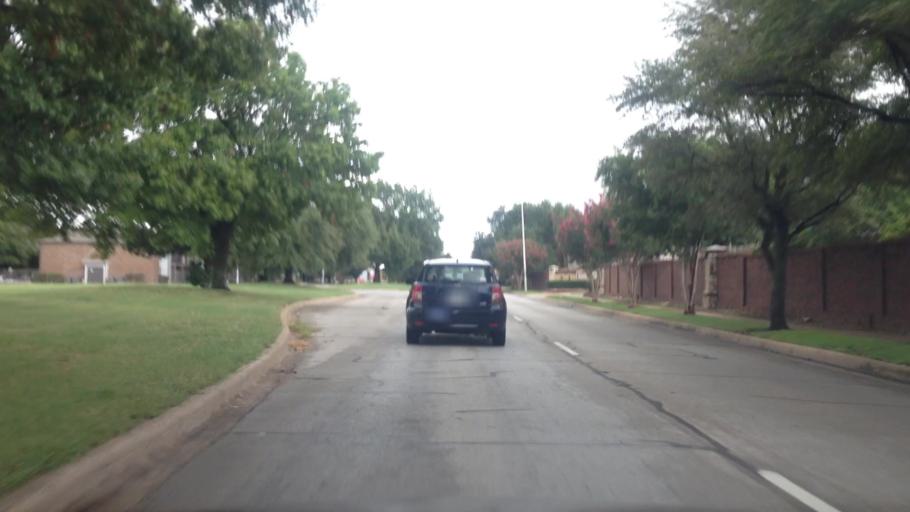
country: US
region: Texas
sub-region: Tarrant County
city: Edgecliff Village
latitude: 32.6365
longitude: -97.3935
